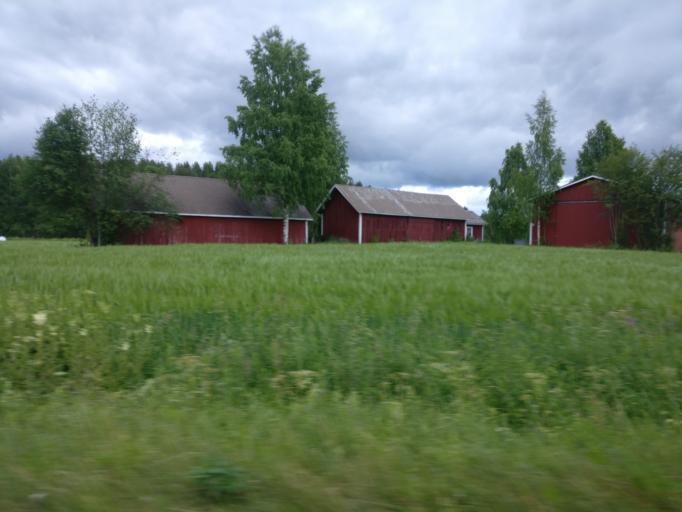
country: FI
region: Northern Savo
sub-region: Varkaus
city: Kangaslampi
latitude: 62.1800
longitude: 28.1073
